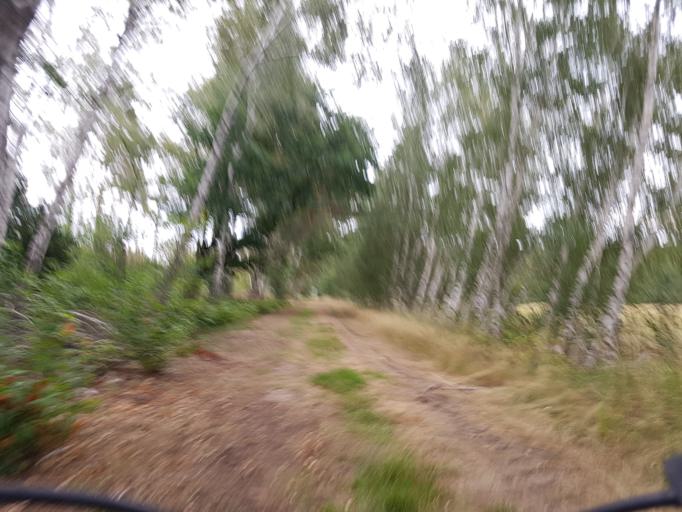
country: DE
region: Brandenburg
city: Trobitz
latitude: 51.5557
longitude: 13.4551
